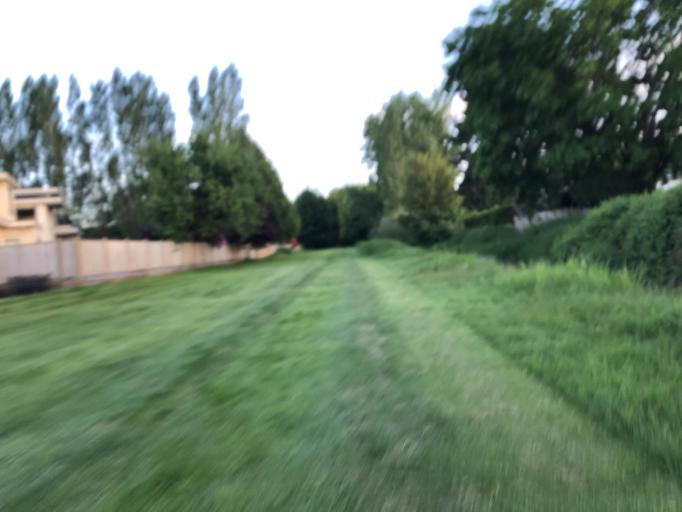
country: CA
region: British Columbia
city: Richmond
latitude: 49.1363
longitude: -123.1253
